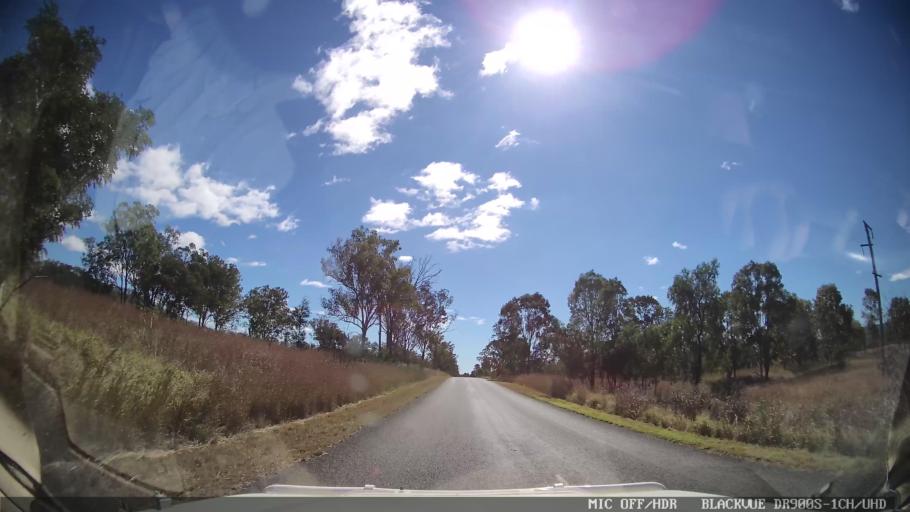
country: AU
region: Queensland
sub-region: Gladstone
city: Toolooa
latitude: -24.4457
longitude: 151.3428
